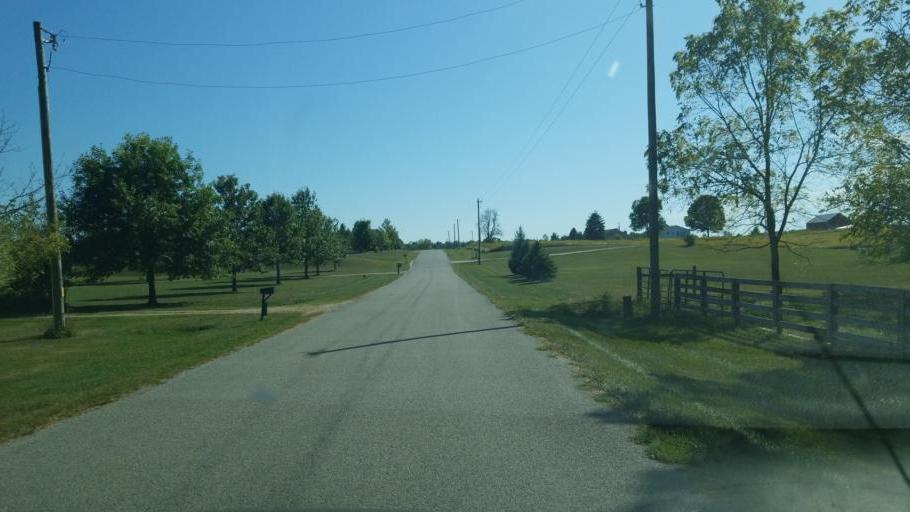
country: US
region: Ohio
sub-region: Champaign County
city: Mechanicsburg
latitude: 40.1214
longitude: -83.6010
